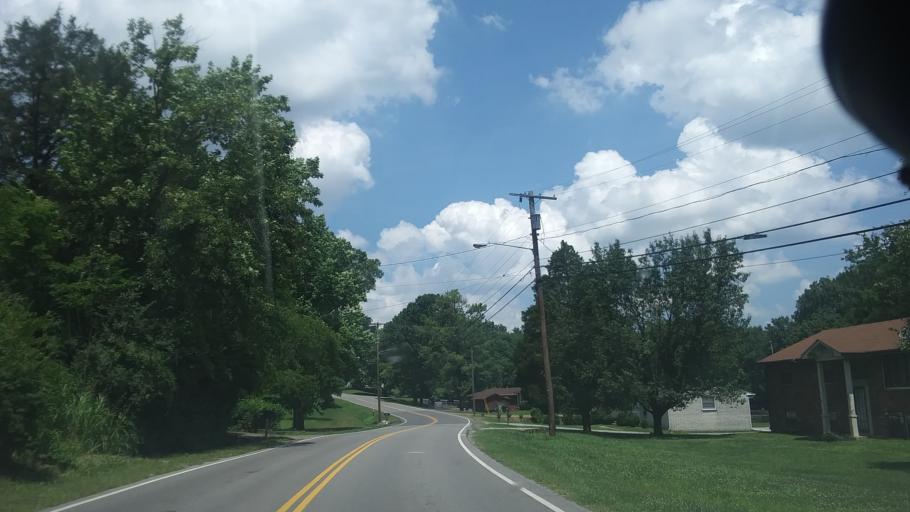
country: US
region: Tennessee
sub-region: Davidson County
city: Oak Hill
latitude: 36.0724
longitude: -86.7000
